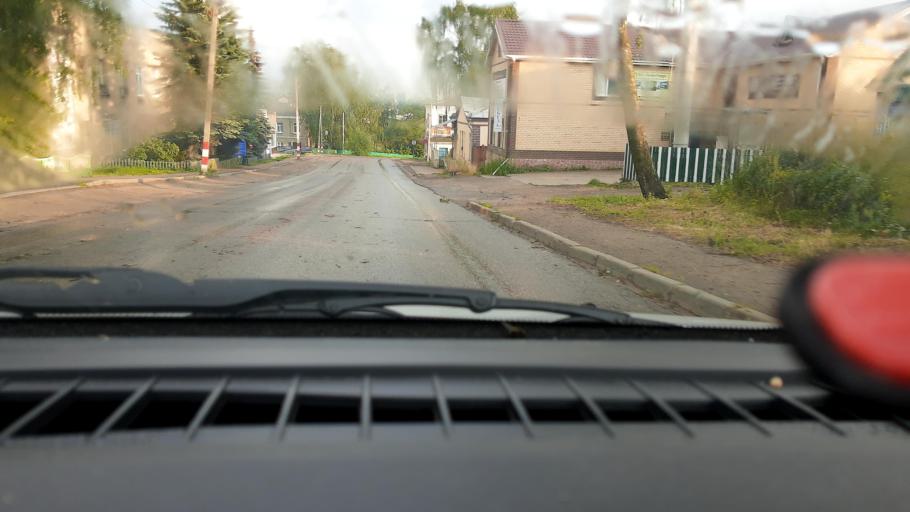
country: RU
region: Nizjnij Novgorod
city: Lukoyanov
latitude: 55.0332
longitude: 44.4949
